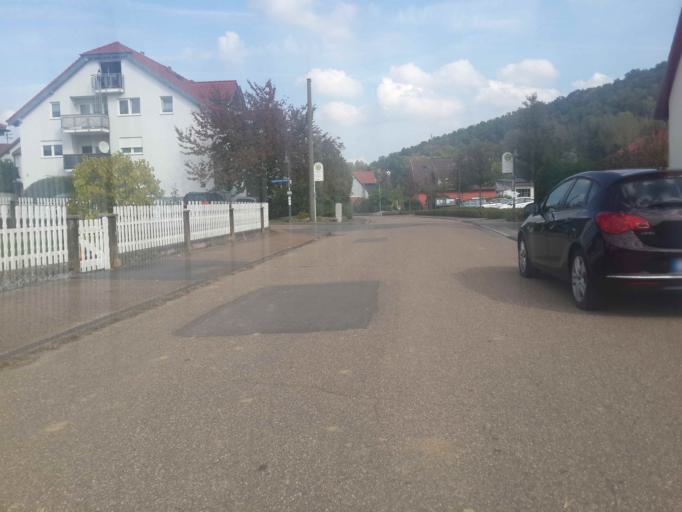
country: DE
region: Baden-Wuerttemberg
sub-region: Regierungsbezirk Stuttgart
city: Jagsthausen
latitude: 49.3086
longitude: 9.4697
